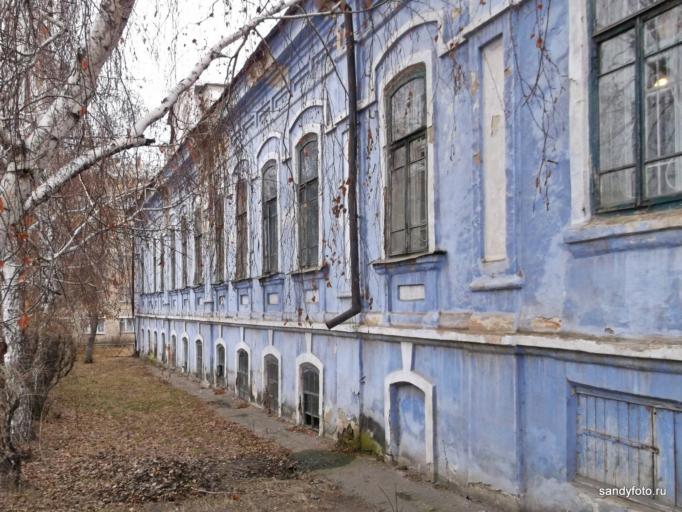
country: RU
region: Chelyabinsk
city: Troitsk
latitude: 54.0791
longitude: 61.5586
